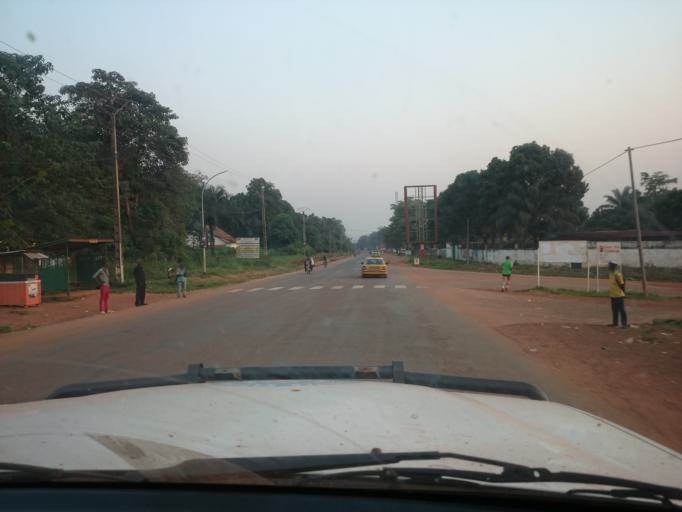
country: CF
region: Bangui
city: Bangui
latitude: 4.3782
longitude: 18.5693
